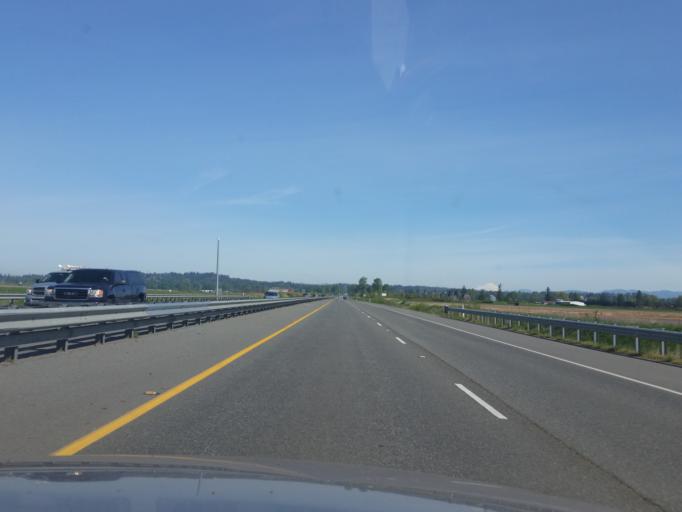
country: US
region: Washington
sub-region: Snohomish County
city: Snohomish
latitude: 47.8841
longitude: -122.1096
